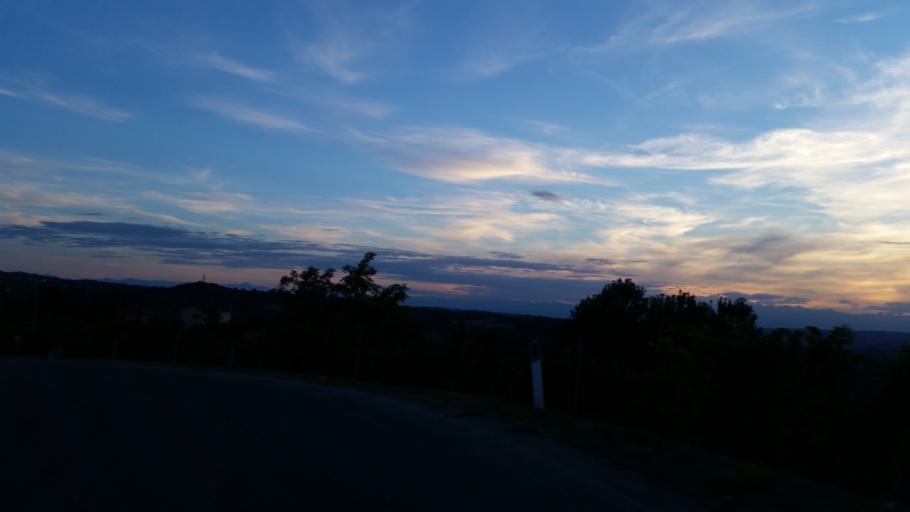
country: IT
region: Piedmont
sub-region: Provincia di Cuneo
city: Castiglione Tinella
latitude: 44.7183
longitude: 8.1844
